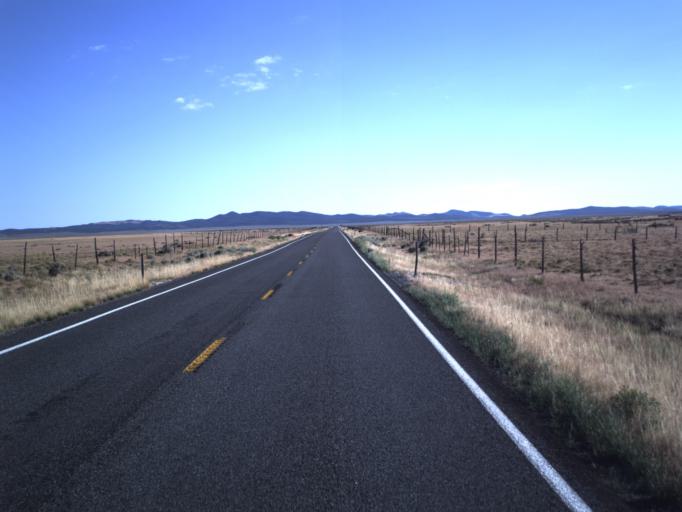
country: US
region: Utah
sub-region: Iron County
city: Enoch
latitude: 37.8963
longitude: -113.0315
